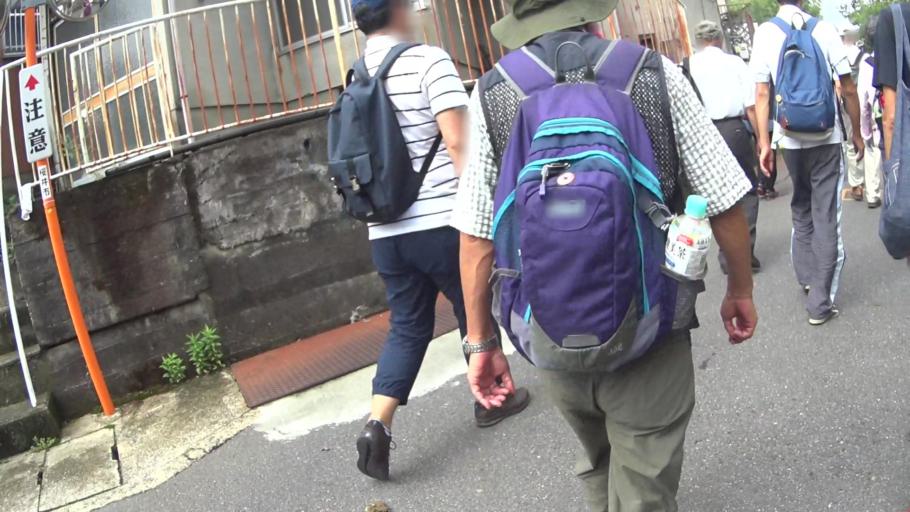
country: JP
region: Nara
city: Sakurai
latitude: 34.5069
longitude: 135.8458
